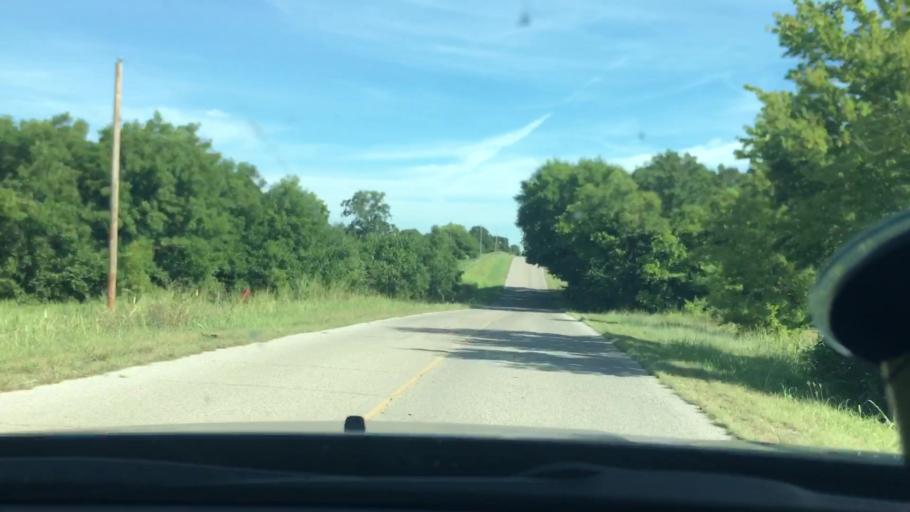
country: US
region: Oklahoma
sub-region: Carter County
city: Lone Grove
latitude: 34.3079
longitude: -97.2824
